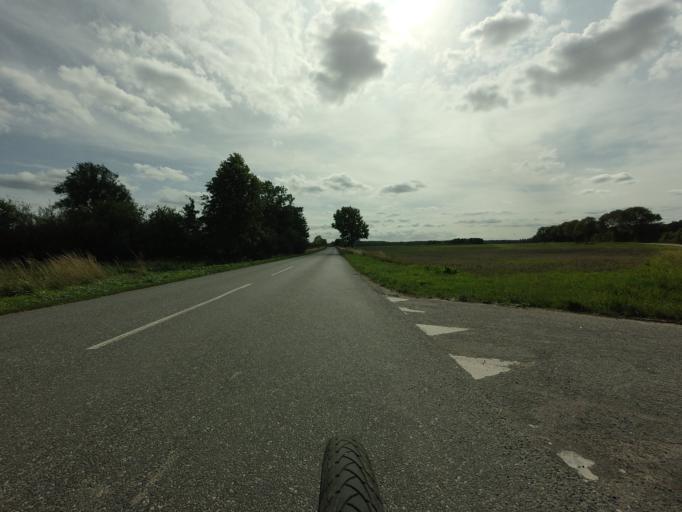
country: DK
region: Zealand
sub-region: Faxe Kommune
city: Fakse Ladeplads
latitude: 55.2509
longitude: 12.2228
